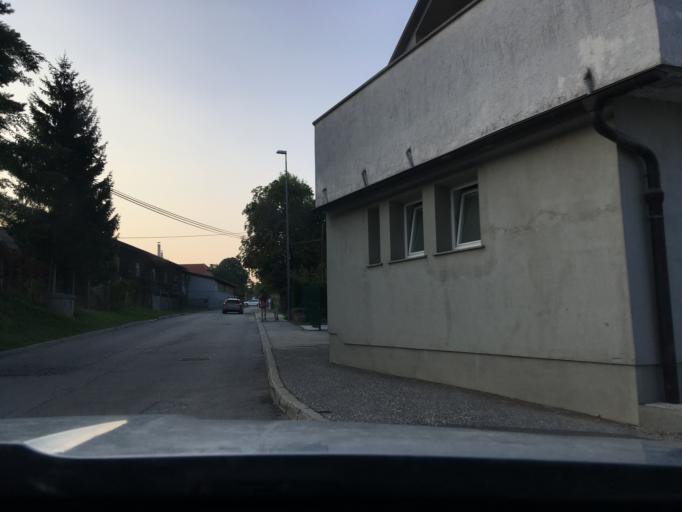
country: SI
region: Kocevje
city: Kocevje
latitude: 45.6429
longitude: 14.8717
